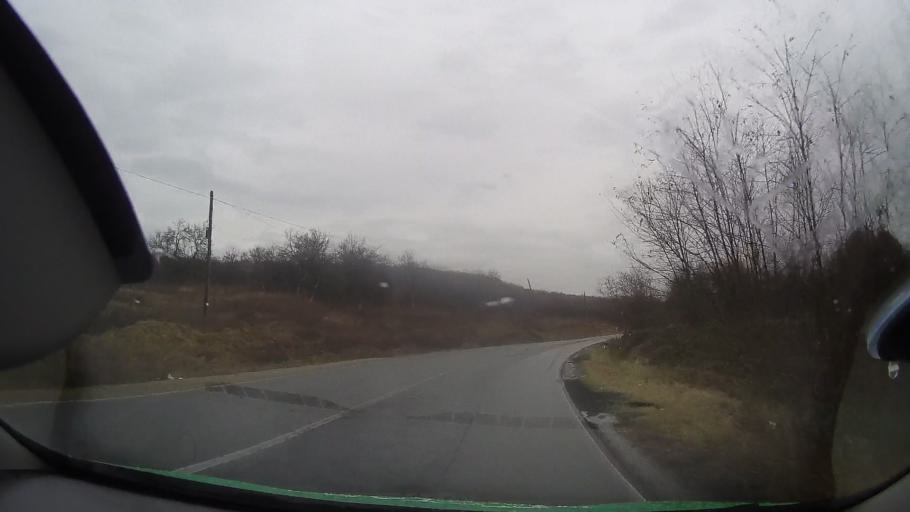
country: RO
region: Bihor
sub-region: Comuna Rabagani
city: Rabagani
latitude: 46.7306
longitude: 22.2326
